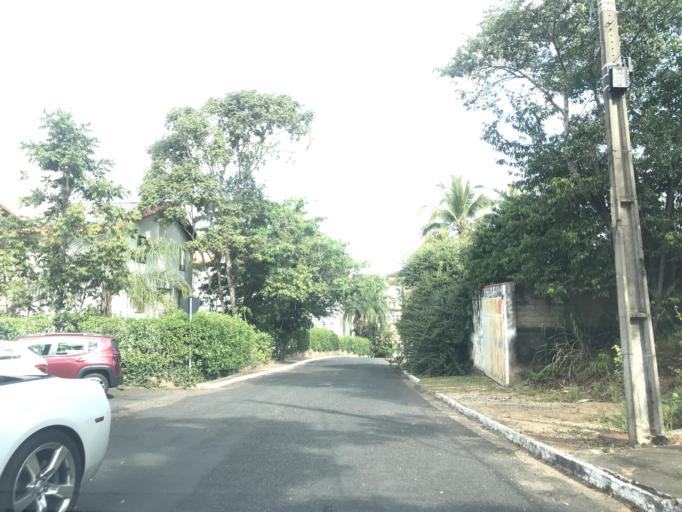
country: BR
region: Goias
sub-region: Caldas Novas
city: Caldas Novas
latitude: -17.7697
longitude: -48.7574
